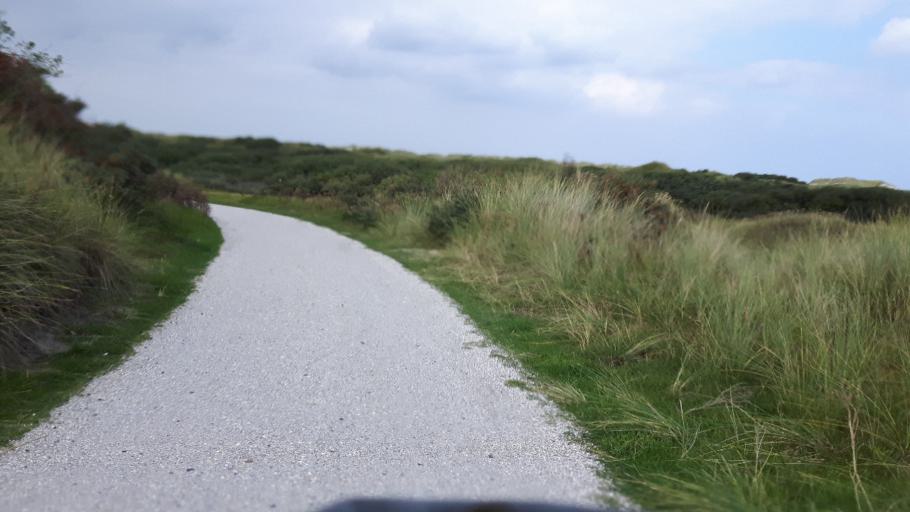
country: NL
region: Friesland
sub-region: Gemeente Dongeradeel
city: Holwerd
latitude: 53.4610
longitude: 5.9002
